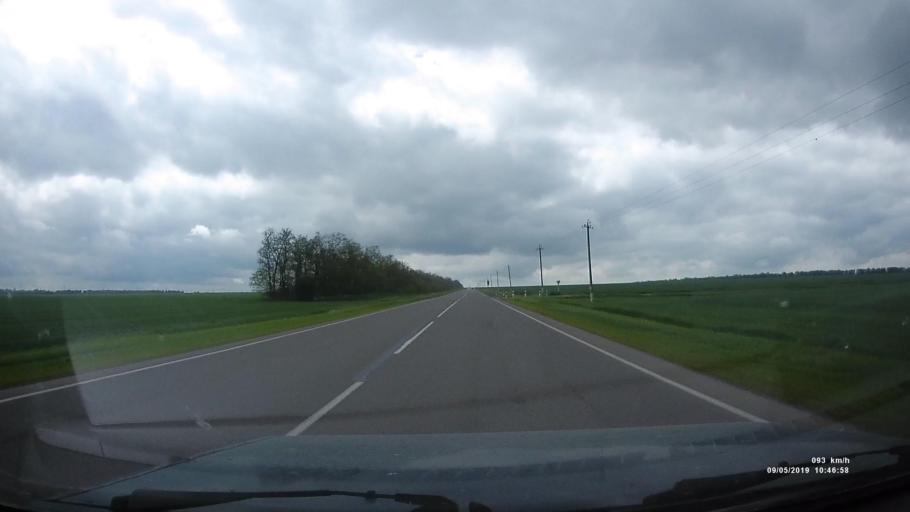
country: RU
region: Rostov
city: Peshkovo
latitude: 46.9772
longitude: 39.3557
